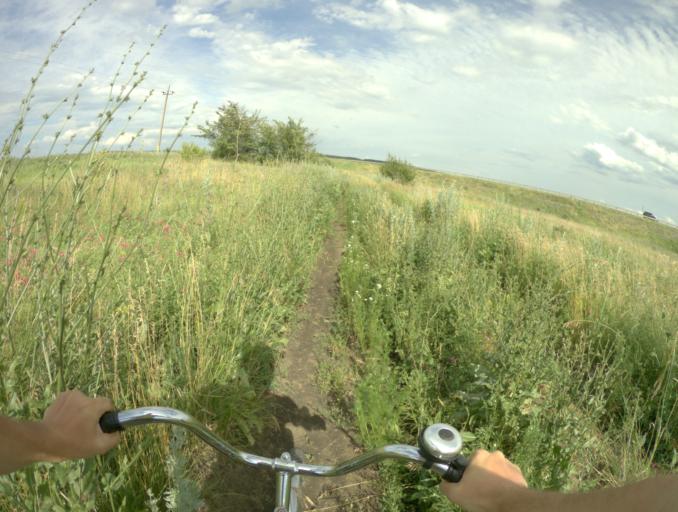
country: RU
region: Saratov
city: Yelshanka
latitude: 51.8447
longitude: 46.4802
